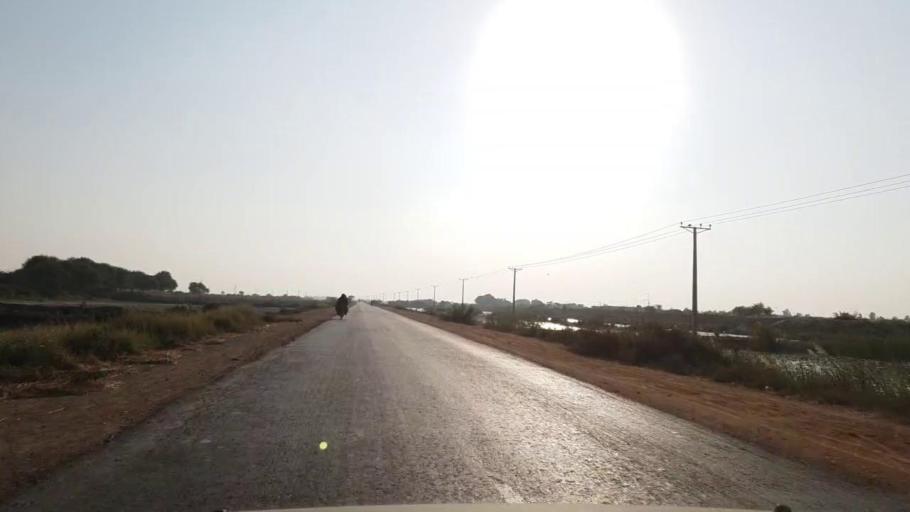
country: PK
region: Sindh
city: Mirpur Batoro
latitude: 24.7610
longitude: 68.2737
